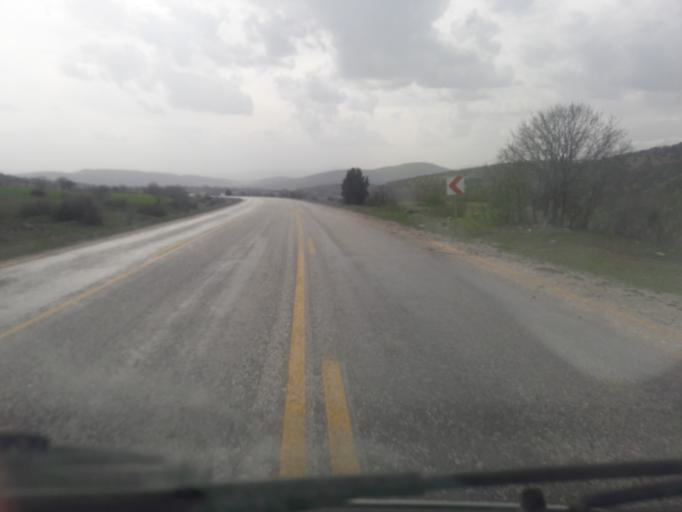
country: TR
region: Gumushane
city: Evren
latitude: 40.1701
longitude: 39.2671
